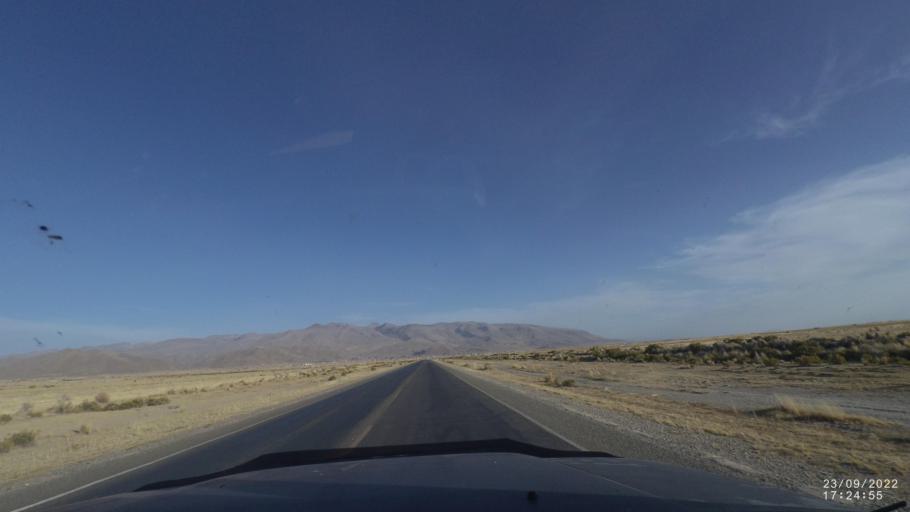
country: BO
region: Oruro
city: Challapata
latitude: -18.8631
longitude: -66.8035
